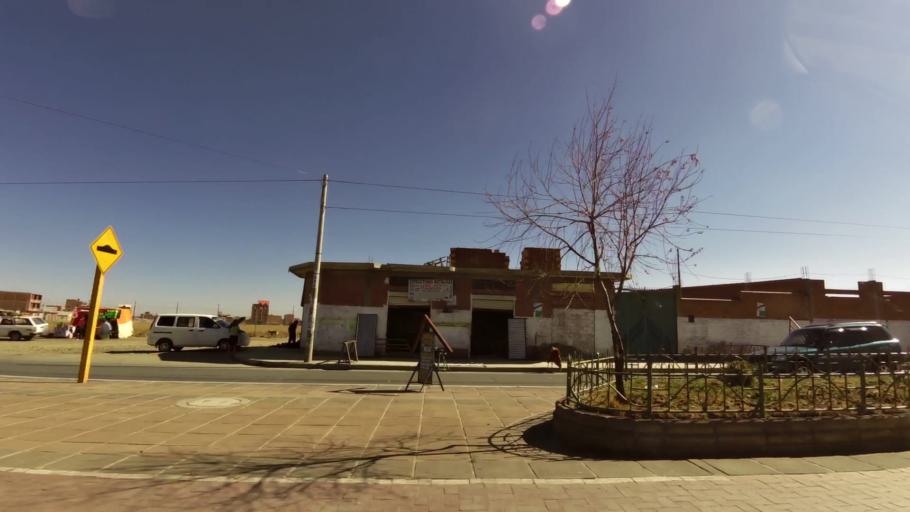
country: BO
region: La Paz
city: La Paz
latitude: -16.5216
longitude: -68.1917
